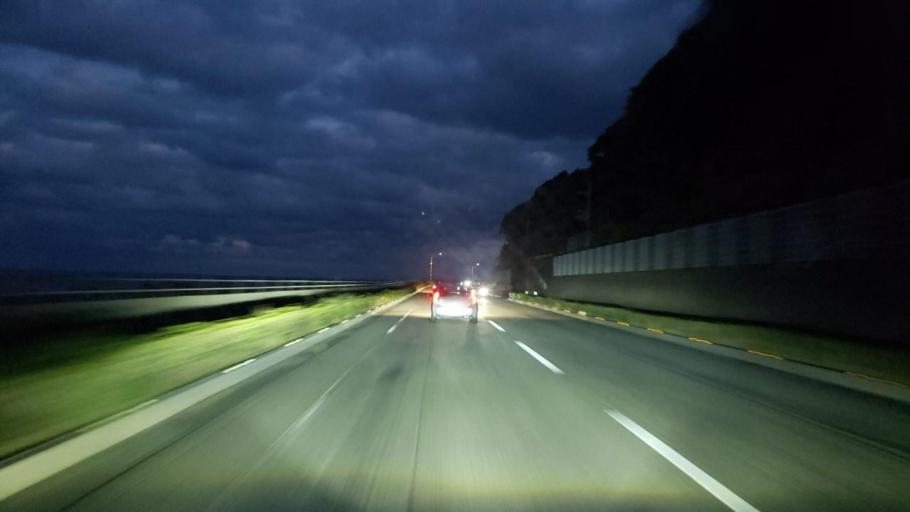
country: JP
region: Tokushima
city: Narutocho-mitsuishi
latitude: 34.2224
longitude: 134.4925
